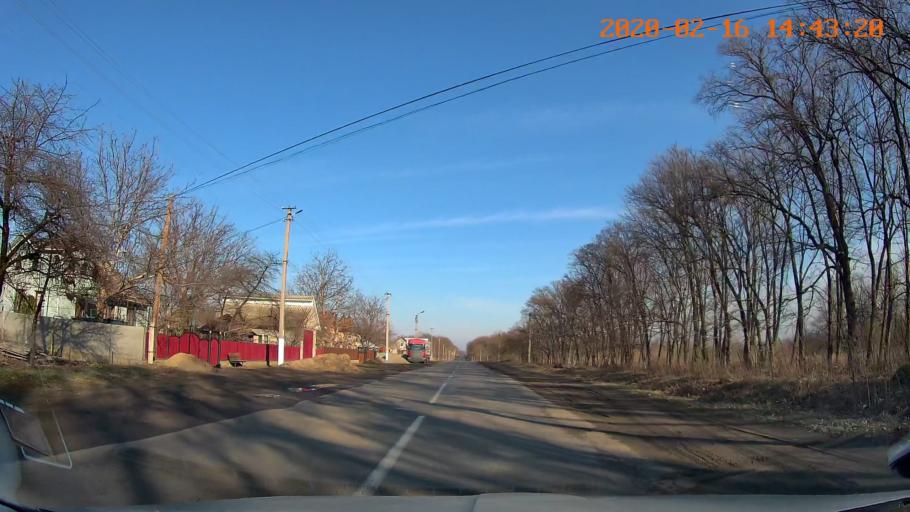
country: RO
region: Botosani
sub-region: Comuna Paltinis
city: Paltinis
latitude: 48.2580
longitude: 26.5974
